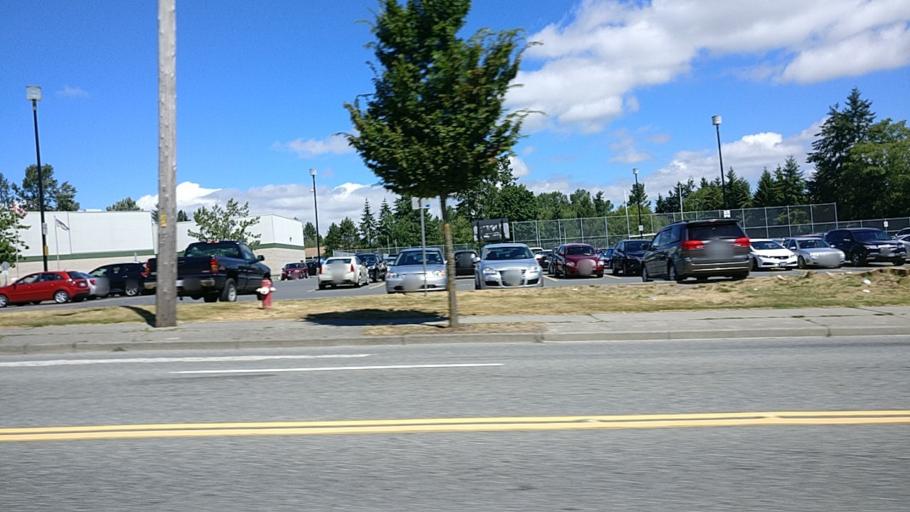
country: CA
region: British Columbia
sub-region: Greater Vancouver Regional District
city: White Rock
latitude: 49.0310
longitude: -122.7843
